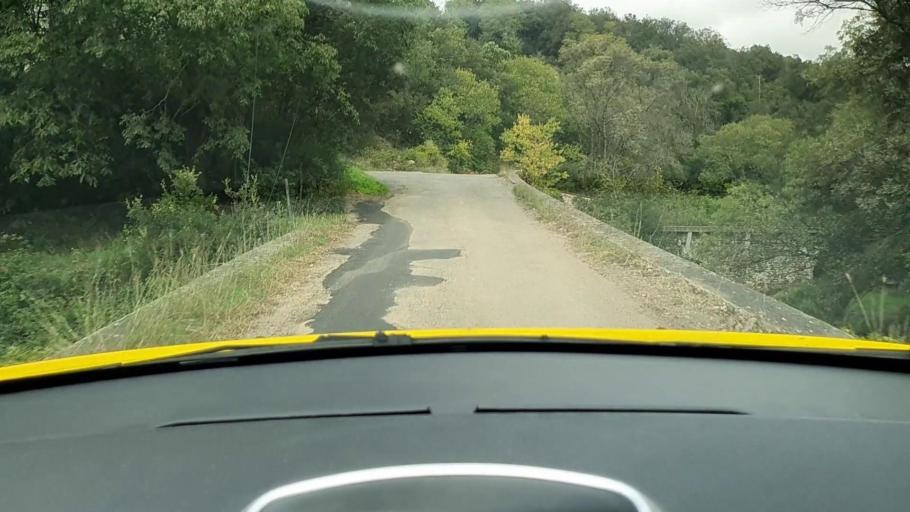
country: FR
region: Languedoc-Roussillon
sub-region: Departement du Gard
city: Sumene
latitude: 44.0065
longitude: 3.6600
